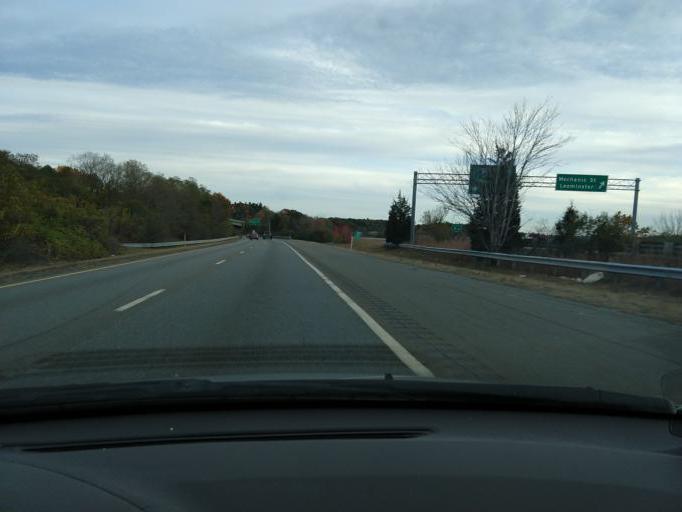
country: US
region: Massachusetts
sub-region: Worcester County
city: Leominster
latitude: 42.5265
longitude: -71.7313
